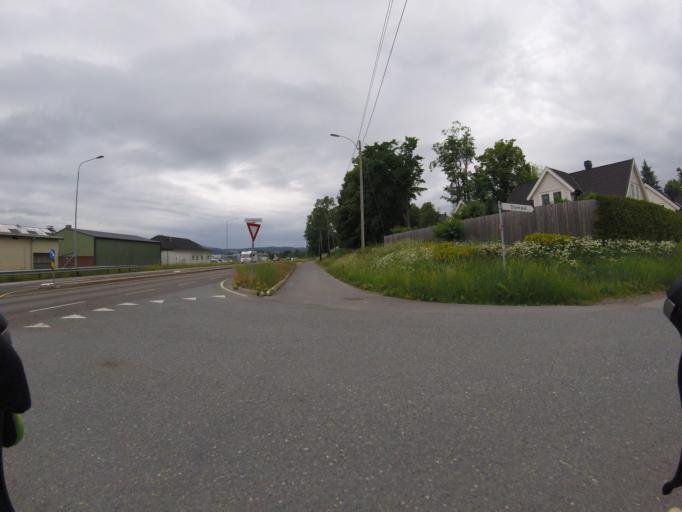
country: NO
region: Akershus
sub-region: Skedsmo
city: Lillestrom
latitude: 59.9745
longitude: 11.0344
